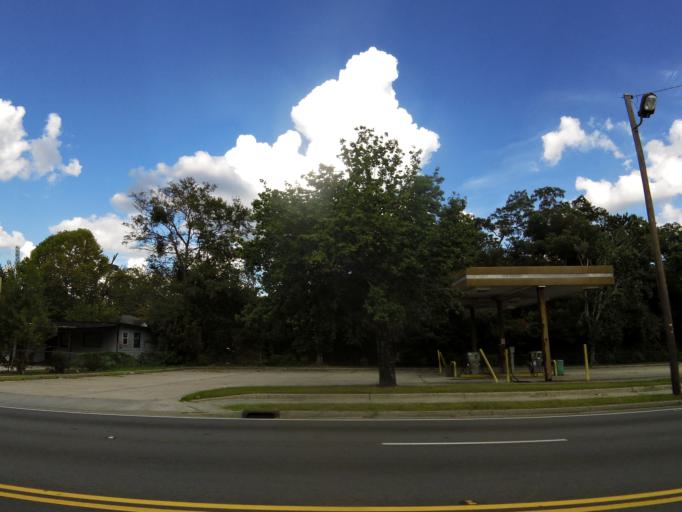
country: US
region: Georgia
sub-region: Lowndes County
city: Valdosta
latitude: 30.8241
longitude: -83.2753
